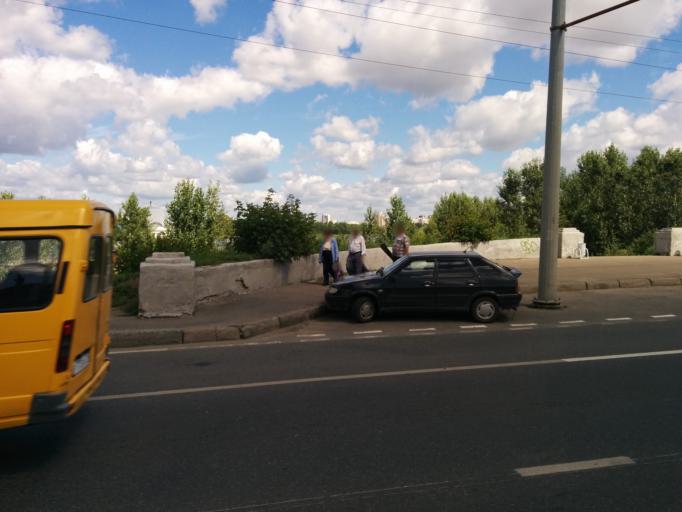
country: RU
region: Tatarstan
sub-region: Gorod Kazan'
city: Kazan
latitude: 55.7985
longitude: 49.0763
